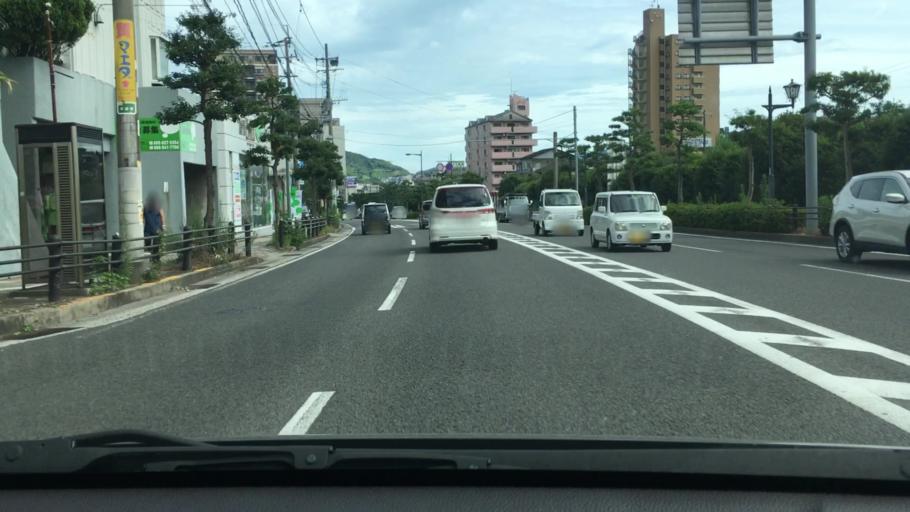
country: JP
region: Nagasaki
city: Obita
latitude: 32.7970
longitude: 129.8547
